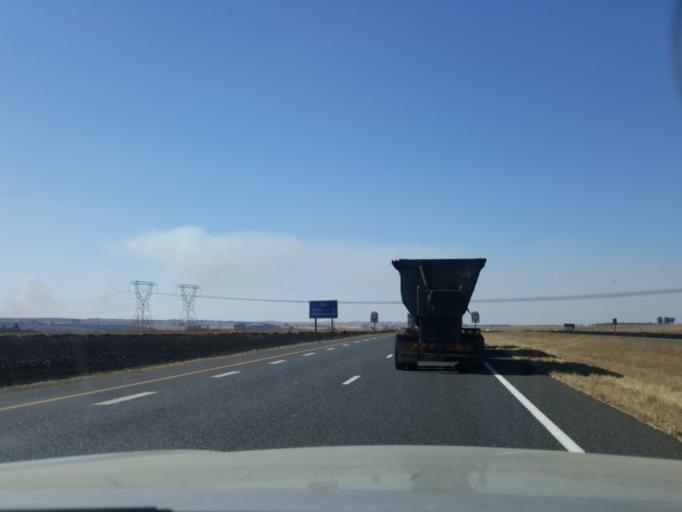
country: ZA
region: Mpumalanga
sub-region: Nkangala District Municipality
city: Delmas
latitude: -26.0219
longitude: 28.8895
